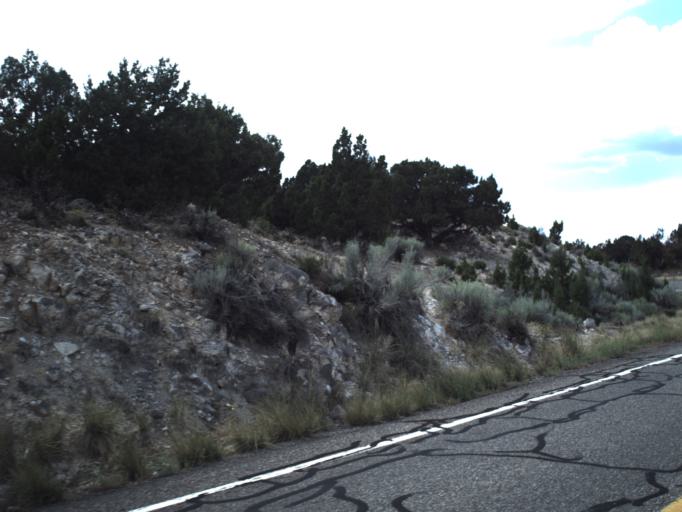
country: US
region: Utah
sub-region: Sevier County
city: Aurora
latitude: 38.7778
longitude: -111.9383
